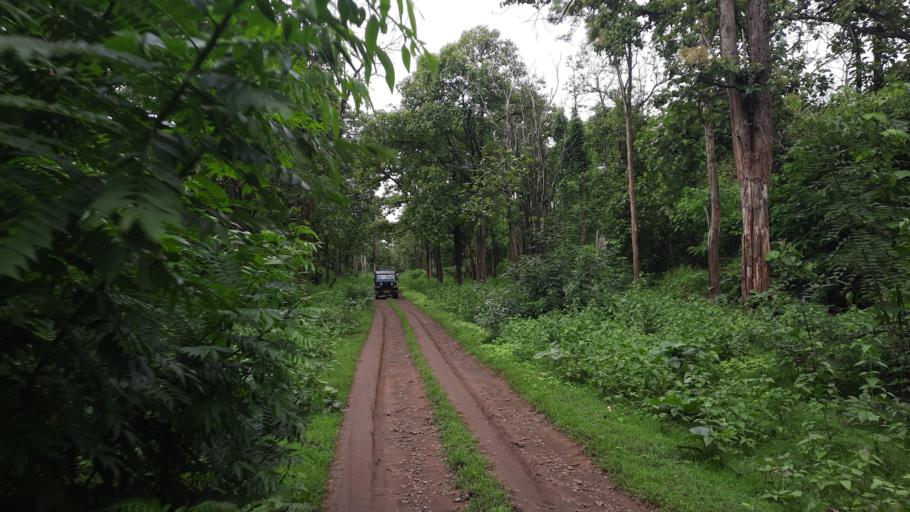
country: IN
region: Kerala
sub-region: Wayanad
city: Panamaram
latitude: 11.9371
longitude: 76.0861
